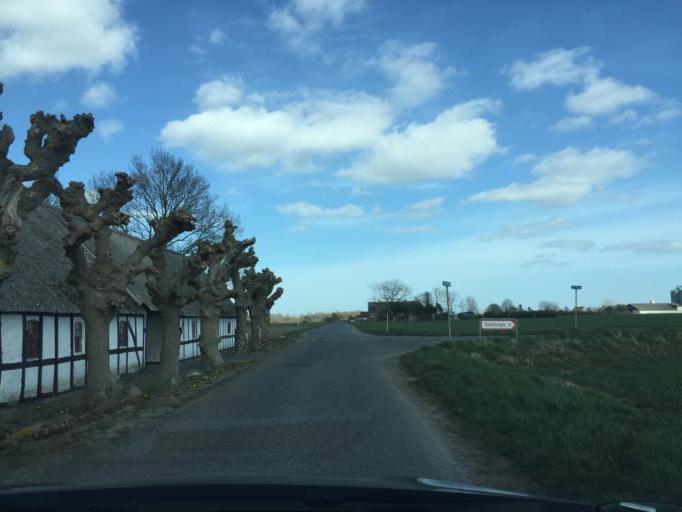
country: DK
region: South Denmark
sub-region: Faaborg-Midtfyn Kommune
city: Arslev
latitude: 55.3094
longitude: 10.5289
